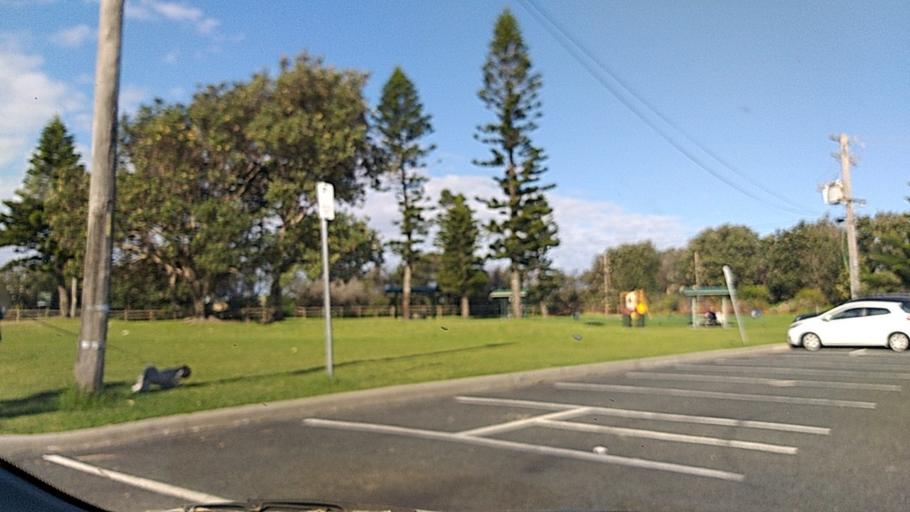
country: AU
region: New South Wales
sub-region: Wollongong
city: Fairy Meadow
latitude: -34.3963
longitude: 150.9047
